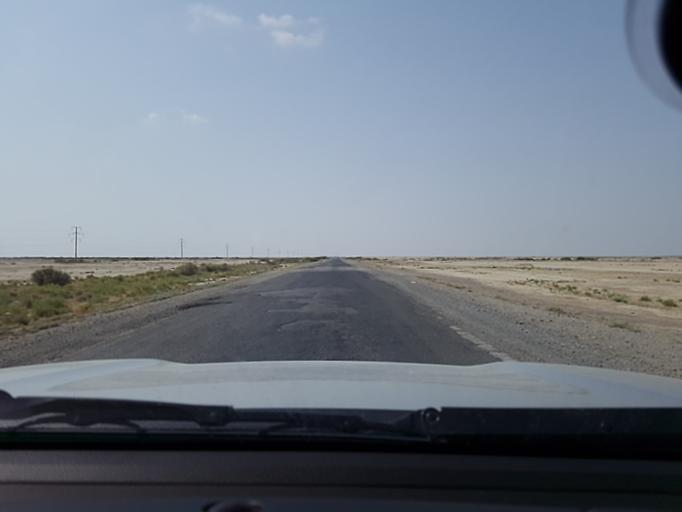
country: TM
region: Balkan
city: Gumdag
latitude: 38.9020
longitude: 54.5922
